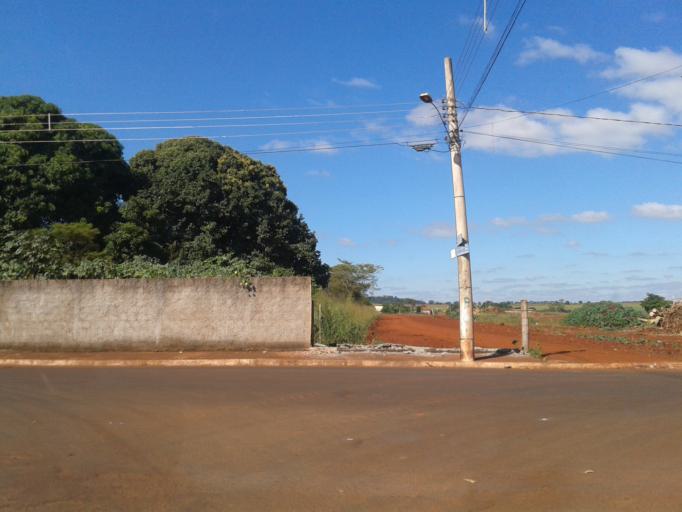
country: BR
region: Minas Gerais
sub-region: Centralina
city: Centralina
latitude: -18.5892
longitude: -49.2029
